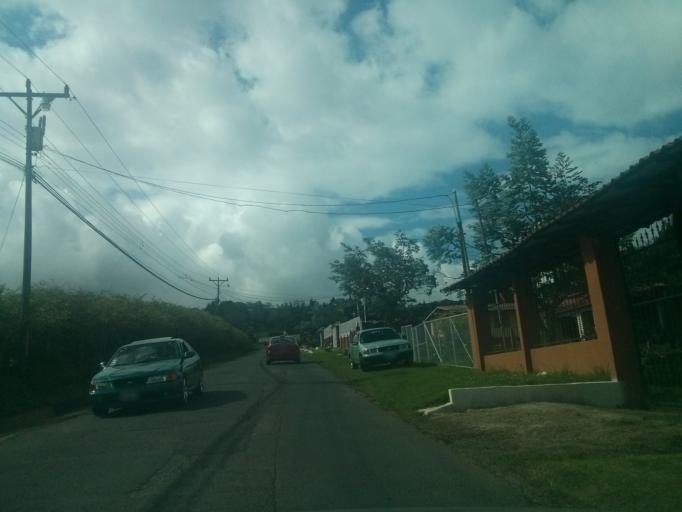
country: CR
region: Alajuela
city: Sabanilla
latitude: 10.1533
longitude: -84.1945
